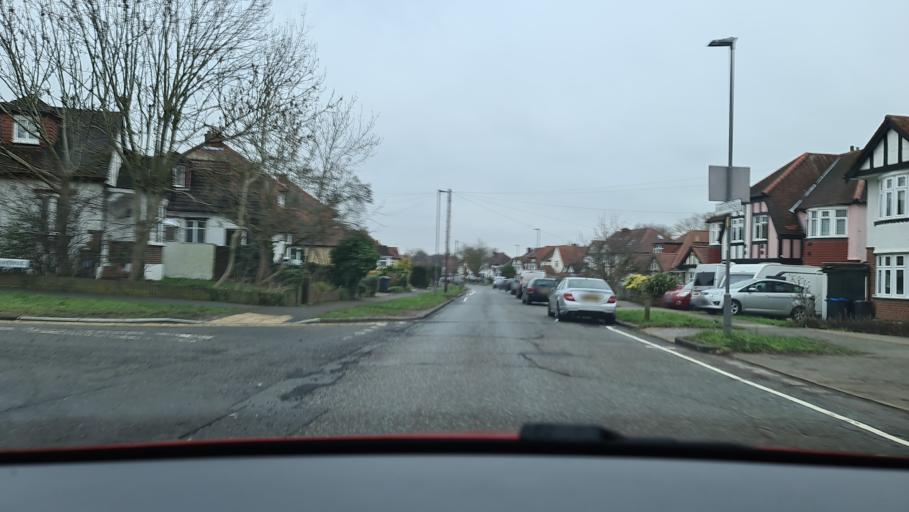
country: GB
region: England
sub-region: Greater London
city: New Malden
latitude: 51.3887
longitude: -0.2718
